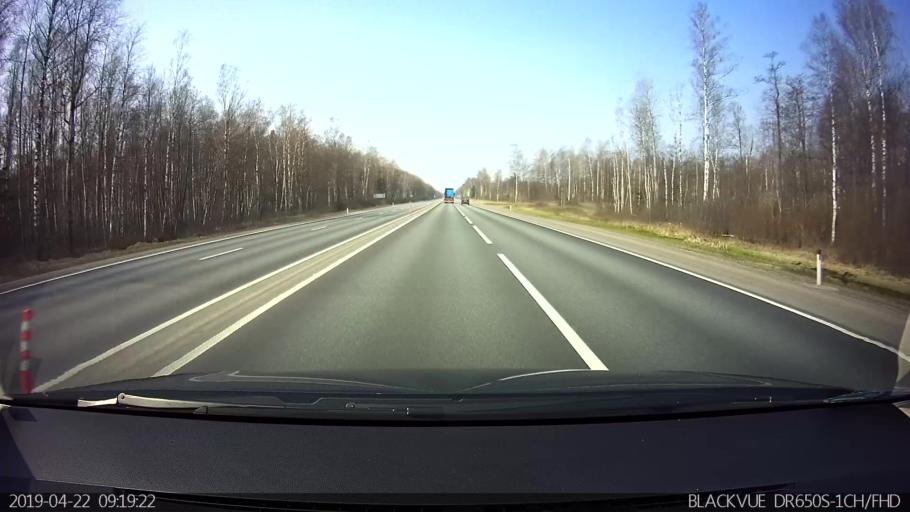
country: RU
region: Smolensk
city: Golynki
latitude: 54.7480
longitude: 31.4656
